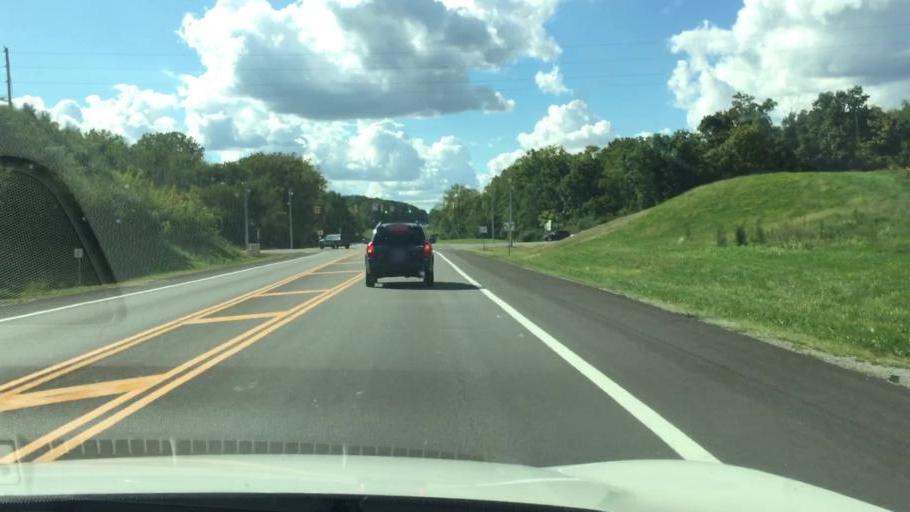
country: US
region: Ohio
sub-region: Clark County
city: Northridge
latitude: 39.9791
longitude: -83.7827
